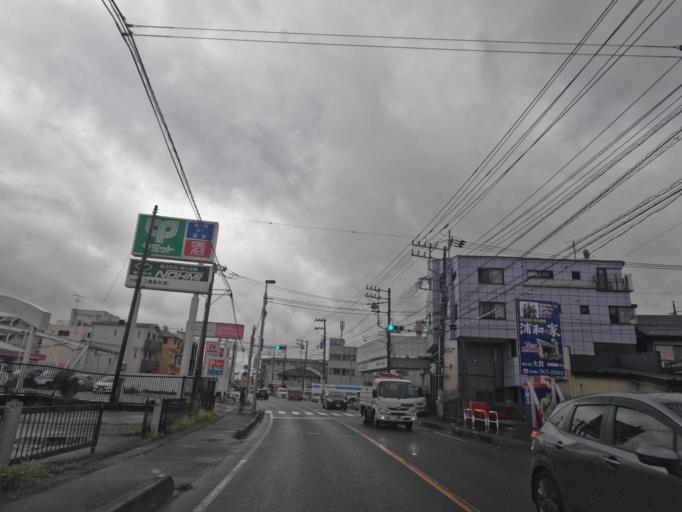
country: JP
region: Saitama
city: Yono
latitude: 35.8609
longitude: 139.6737
